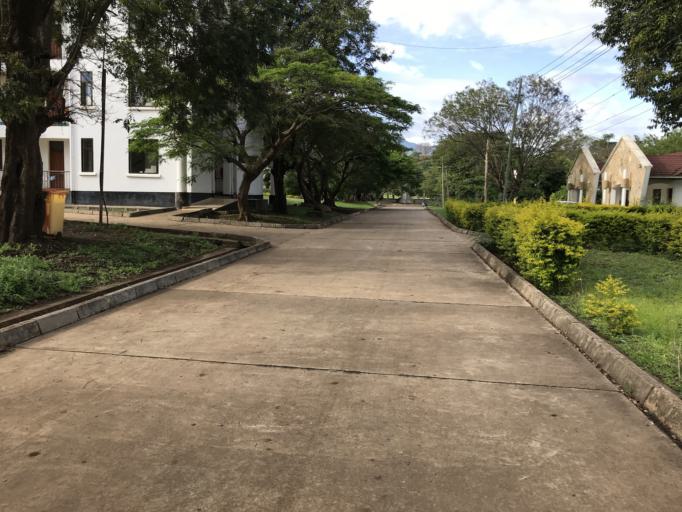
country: TZ
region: Arusha
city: Usa River
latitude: -3.3993
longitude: 36.8012
